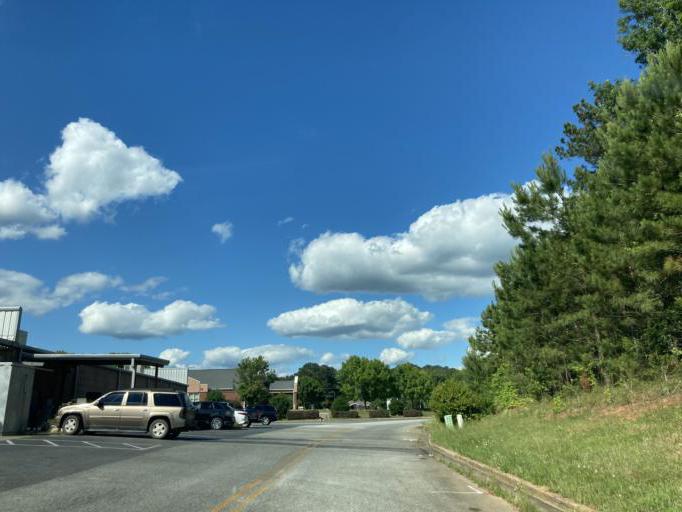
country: US
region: Georgia
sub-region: Jones County
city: Gray
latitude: 33.0013
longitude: -83.5473
